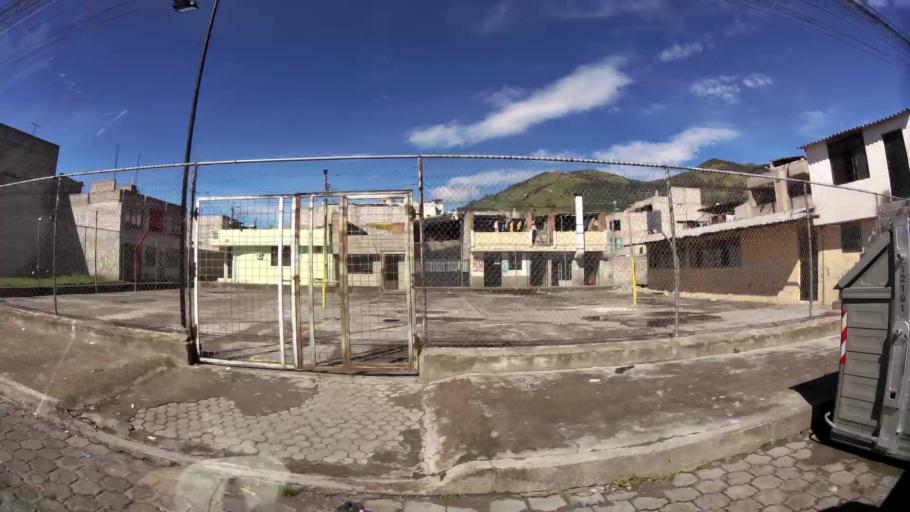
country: EC
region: Pichincha
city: Quito
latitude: -0.2997
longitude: -78.5652
